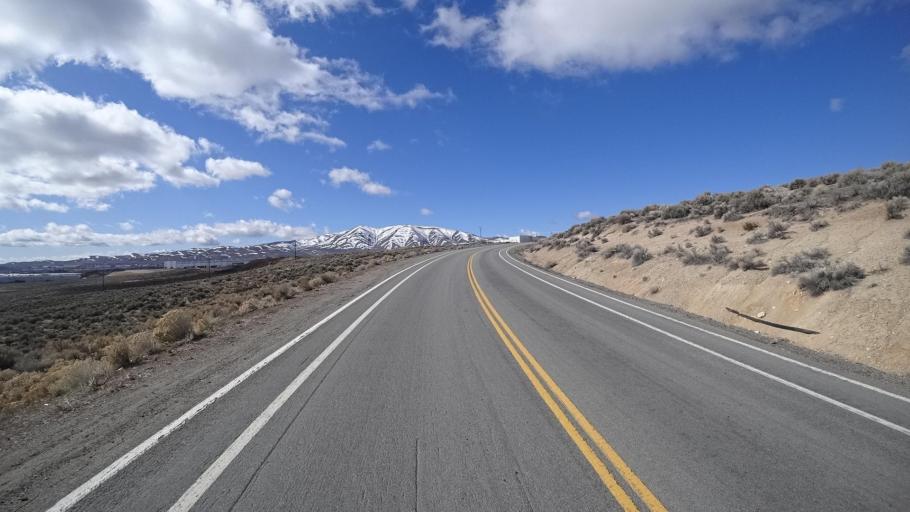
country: US
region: Nevada
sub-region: Washoe County
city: Lemmon Valley
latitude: 39.6576
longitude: -119.8659
